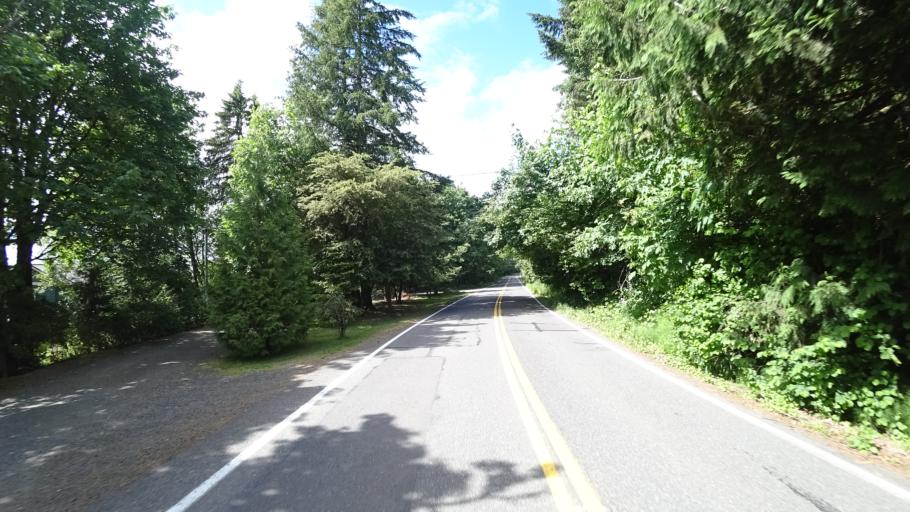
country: US
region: Oregon
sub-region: Washington County
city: Bethany
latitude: 45.6003
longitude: -122.8326
